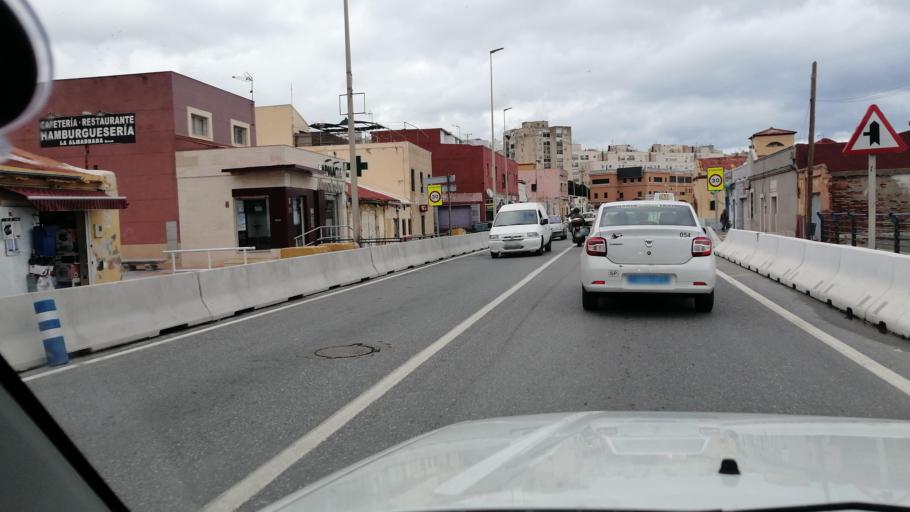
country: ES
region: Ceuta
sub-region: Ceuta
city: Ceuta
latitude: 35.8792
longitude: -5.3369
